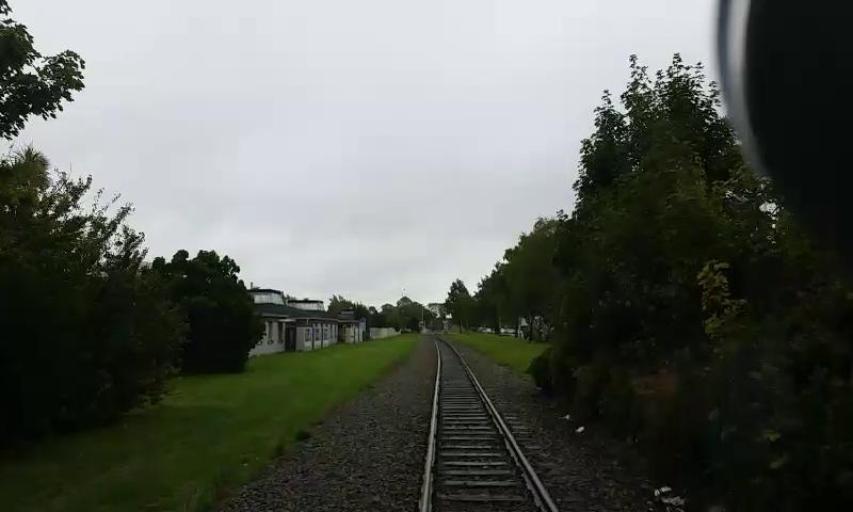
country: NZ
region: Canterbury
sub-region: Christchurch City
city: Christchurch
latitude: -43.5284
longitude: 172.6086
